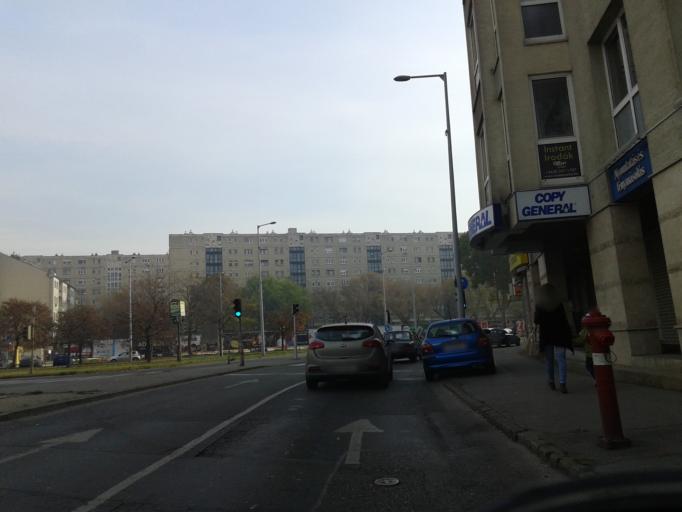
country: HU
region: Budapest
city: Budapest III. keruelet
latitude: 47.5319
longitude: 19.0392
